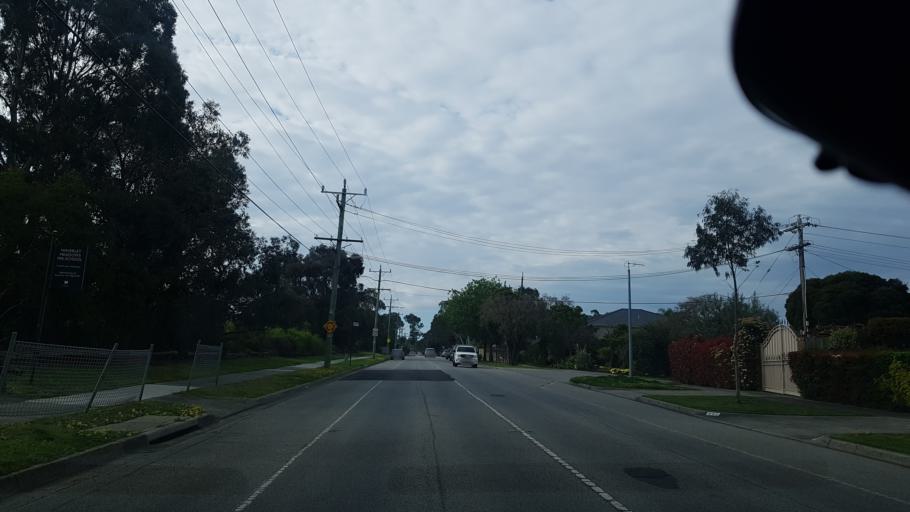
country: AU
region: Victoria
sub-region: Monash
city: Mulgrave
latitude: -37.9126
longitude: 145.1784
